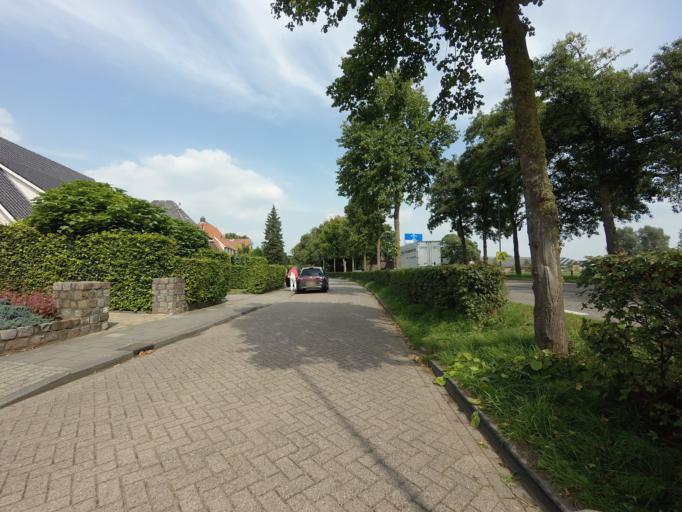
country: NL
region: Gelderland
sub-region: Oude IJsselstreek
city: Gendringen
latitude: 51.8734
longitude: 6.3838
